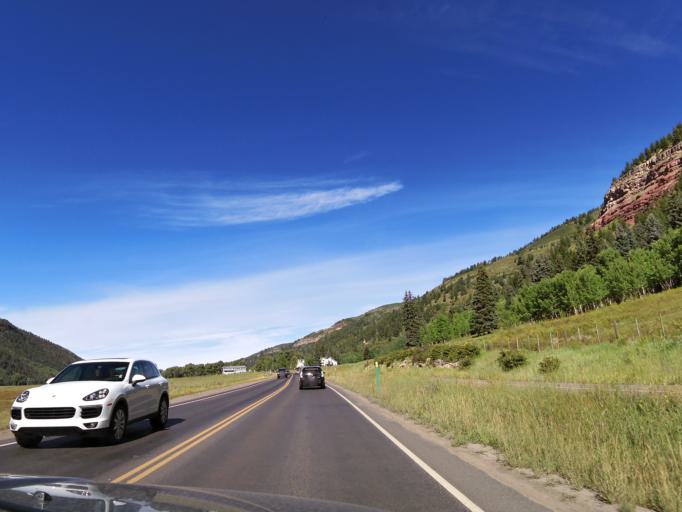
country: US
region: Colorado
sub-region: San Miguel County
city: Telluride
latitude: 37.9452
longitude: -107.8293
